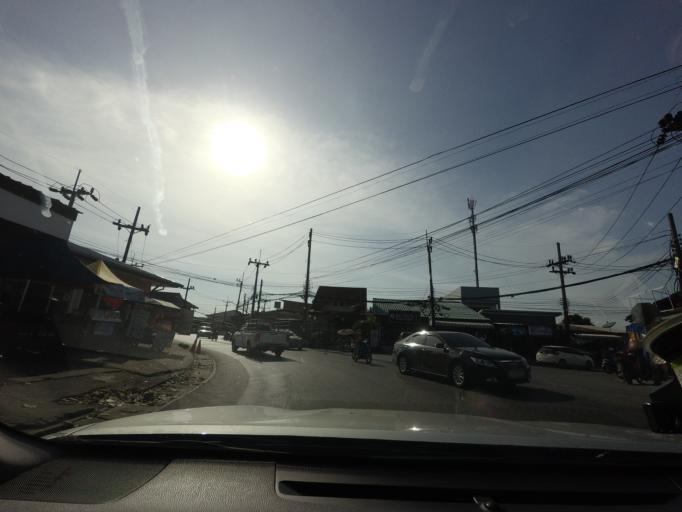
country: TH
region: Phuket
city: Thalang
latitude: 8.0166
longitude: 98.3204
